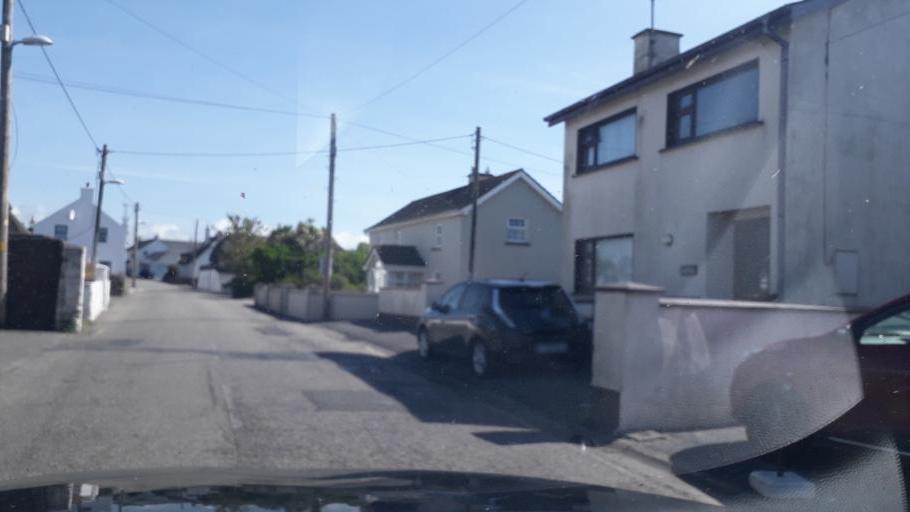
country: IE
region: Leinster
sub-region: Loch Garman
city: Loch Garman
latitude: 52.1761
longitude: -6.5858
